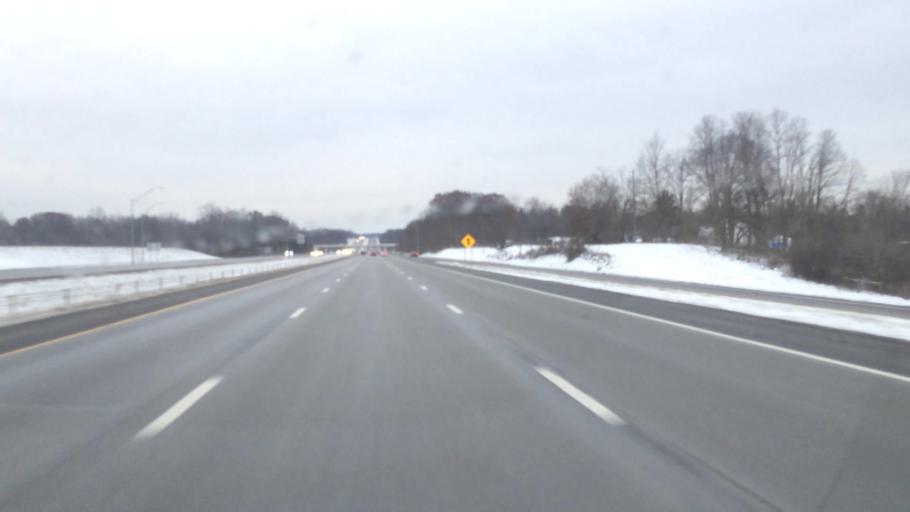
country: US
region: Ohio
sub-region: Medina County
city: Brunswick
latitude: 41.1920
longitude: -81.7907
